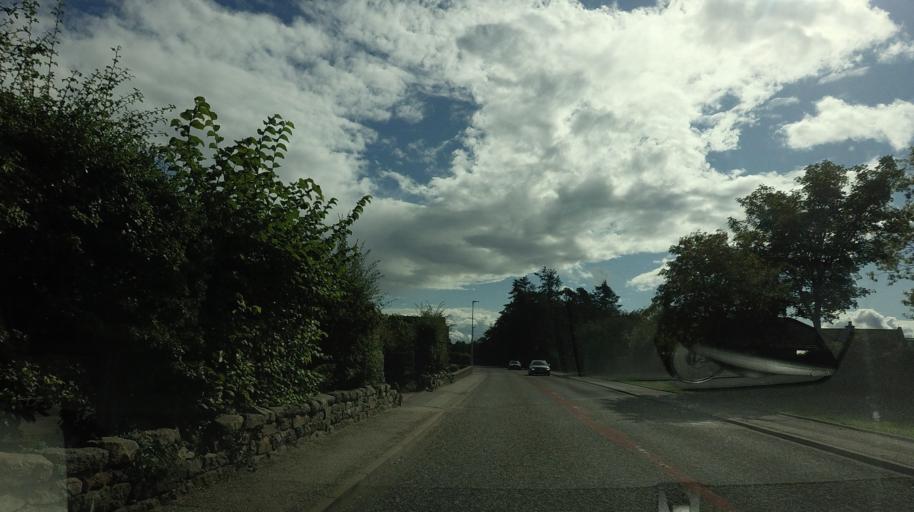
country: GB
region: Scotland
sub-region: Aberdeenshire
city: Torphins
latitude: 57.1033
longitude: -2.6195
